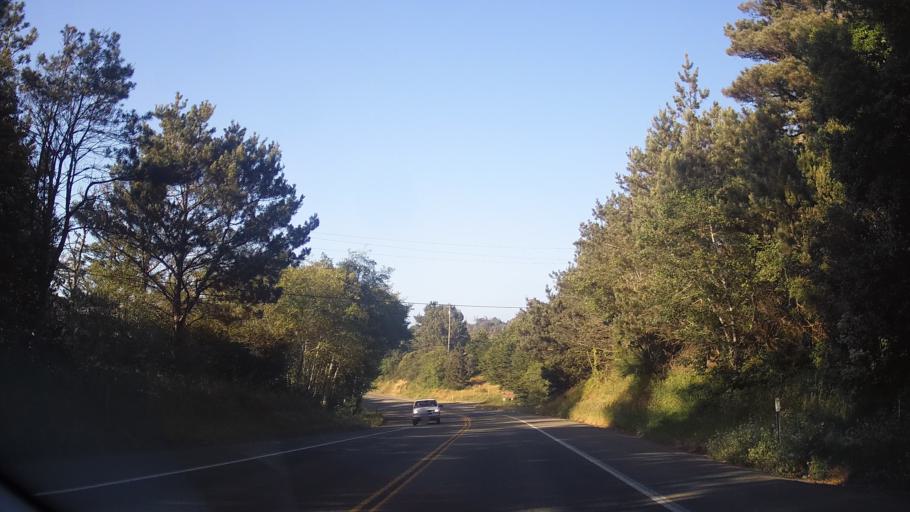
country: US
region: California
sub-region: Mendocino County
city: Fort Bragg
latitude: 39.4858
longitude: -123.7892
